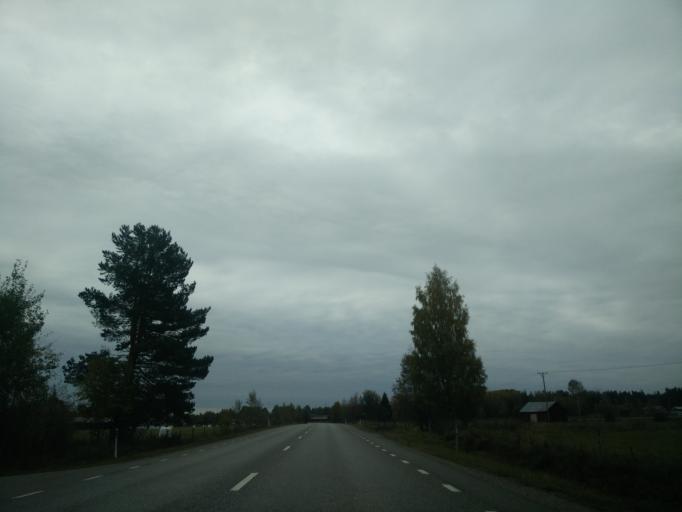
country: SE
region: Gaevleborg
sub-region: Gavle Kommun
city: Norrsundet
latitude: 60.9016
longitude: 17.0506
